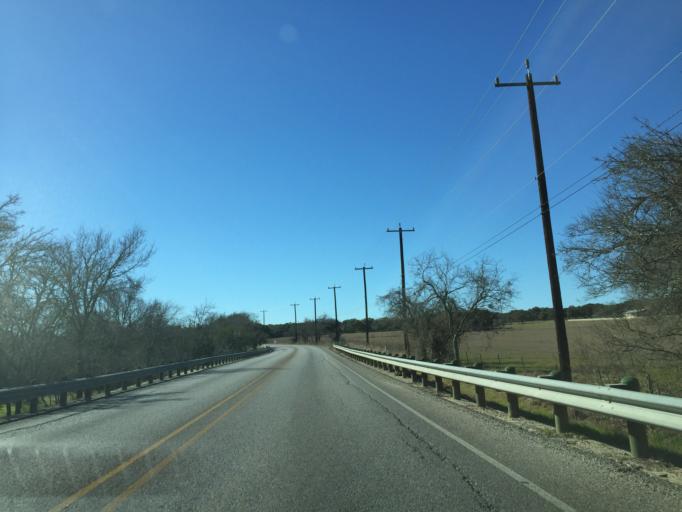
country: US
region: Texas
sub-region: Comal County
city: Bulverde
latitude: 29.7441
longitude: -98.4224
